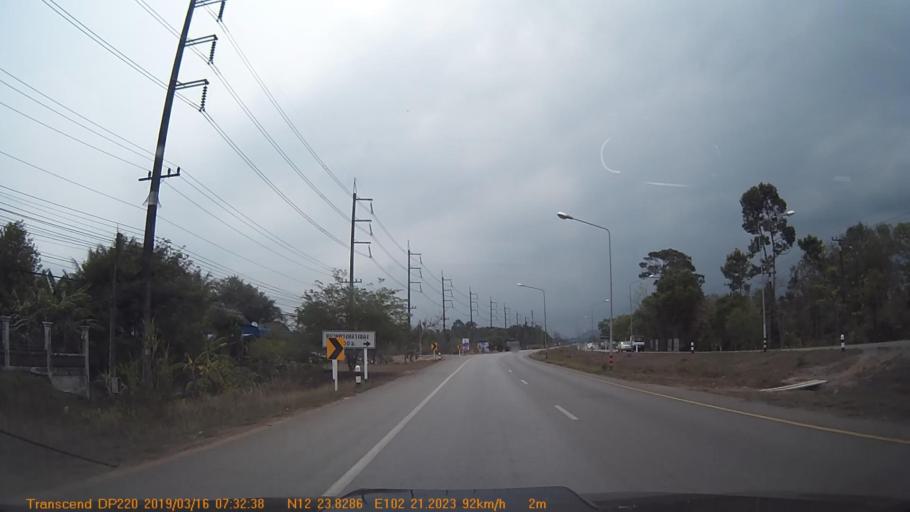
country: TH
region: Trat
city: Khao Saming
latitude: 12.3913
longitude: 102.3662
